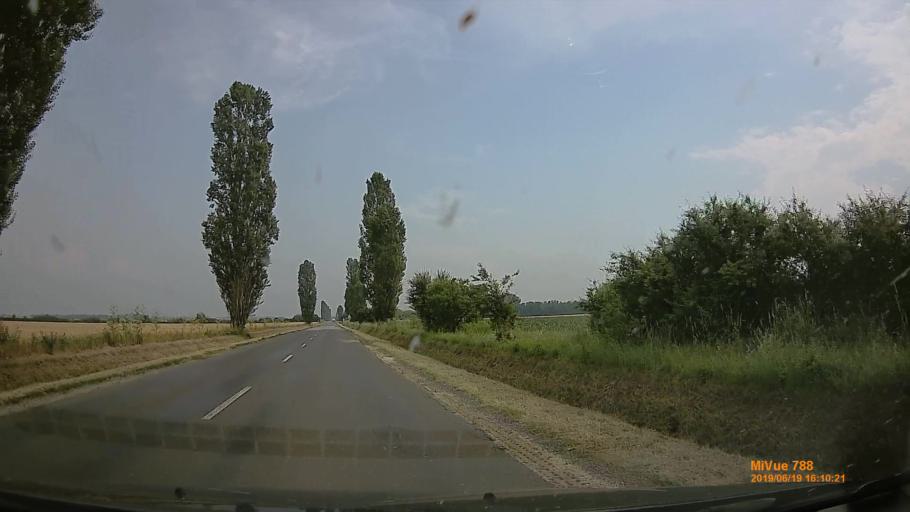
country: HU
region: Baranya
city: Szigetvar
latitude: 46.0705
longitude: 17.7666
